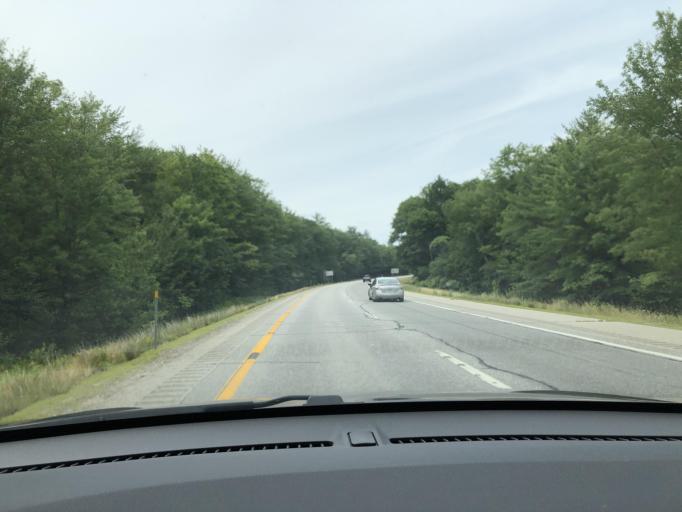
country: US
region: New Hampshire
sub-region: Merrimack County
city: Sutton
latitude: 43.3199
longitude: -71.8888
